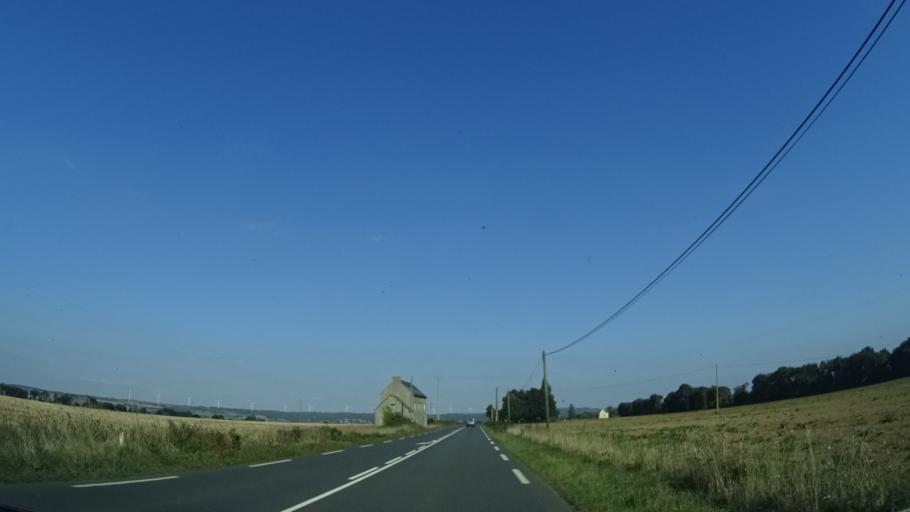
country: FR
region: Brittany
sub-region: Departement du Finistere
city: Cast
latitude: 48.1389
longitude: -4.1783
